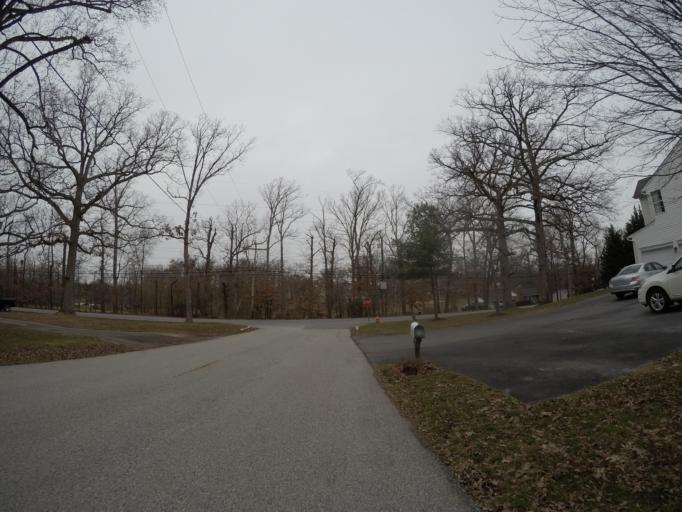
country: US
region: Maryland
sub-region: Howard County
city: Ilchester
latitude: 39.2273
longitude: -76.7858
